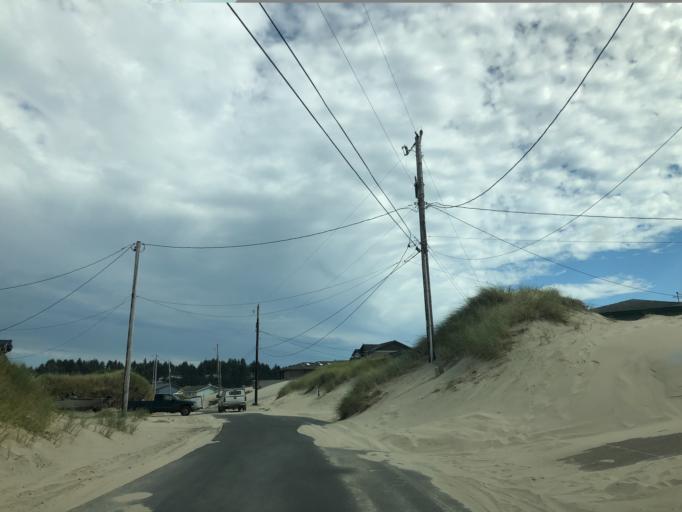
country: US
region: Oregon
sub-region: Lincoln County
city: Waldport
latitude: 44.4270
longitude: -124.0814
